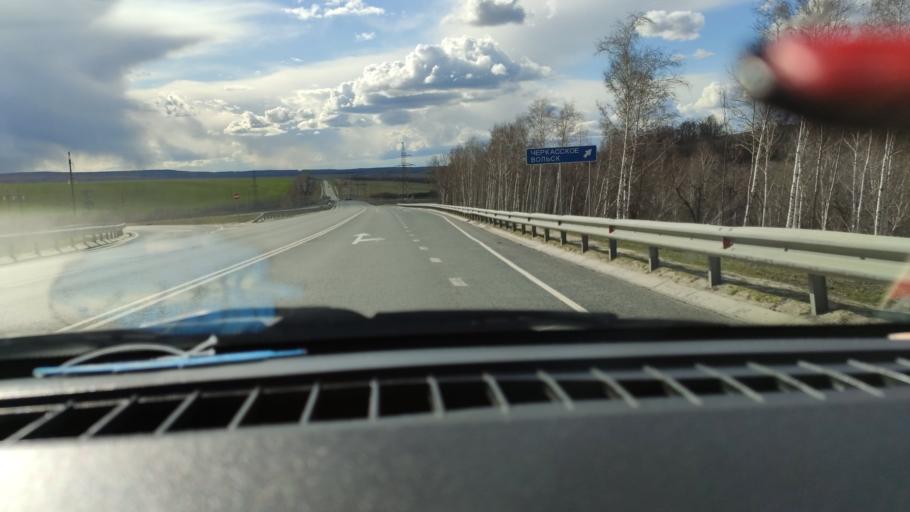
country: RU
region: Saratov
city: Vol'sk
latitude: 52.1145
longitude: 47.3053
